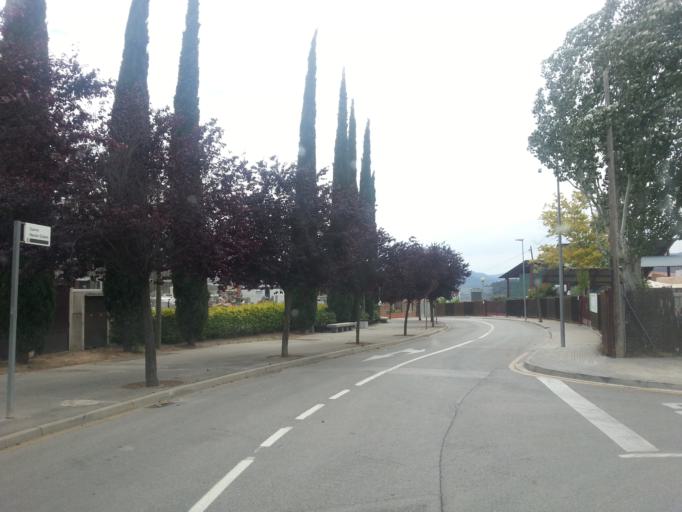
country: ES
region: Catalonia
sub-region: Provincia de Barcelona
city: Molins de Rei
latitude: 41.4200
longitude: 2.0184
